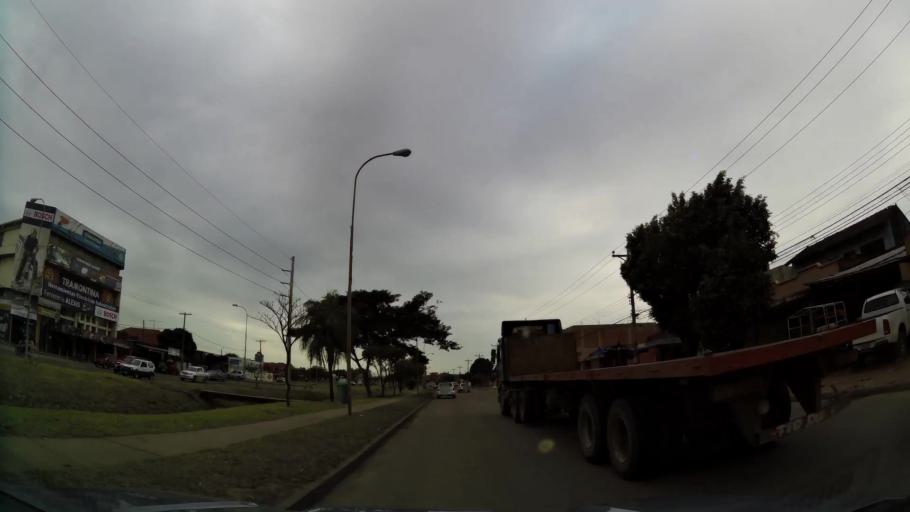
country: BO
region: Santa Cruz
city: Santa Cruz de la Sierra
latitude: -17.7963
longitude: -63.1492
